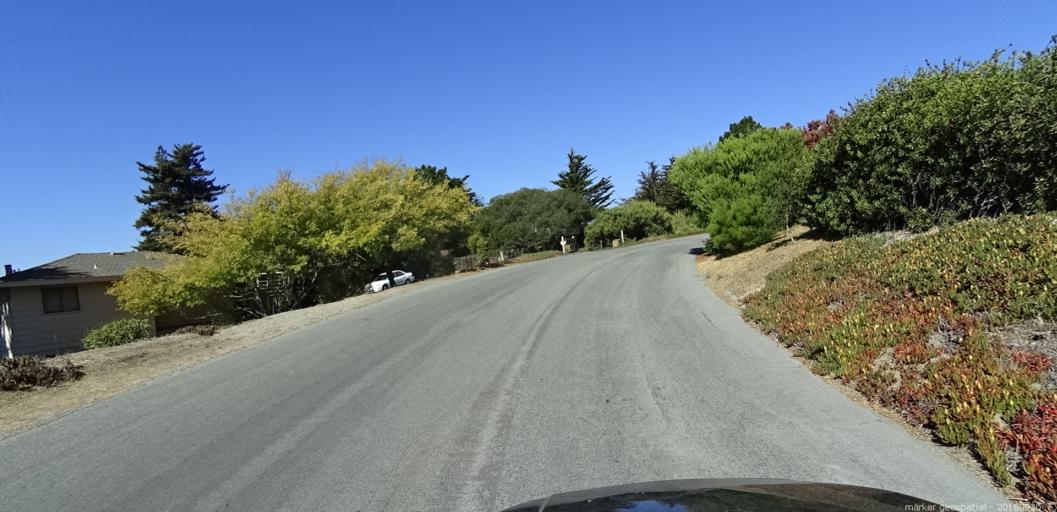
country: US
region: California
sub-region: Monterey County
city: Carmel-by-the-Sea
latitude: 36.5451
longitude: -121.9015
